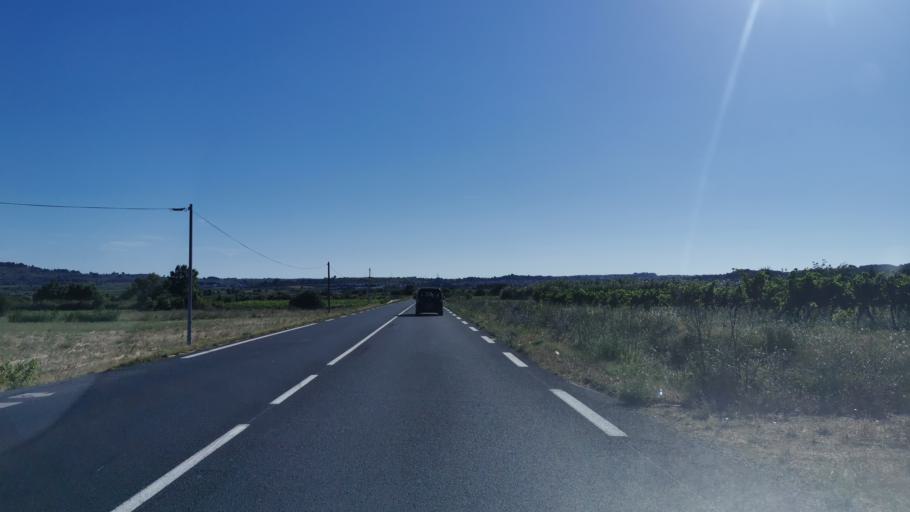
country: FR
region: Languedoc-Roussillon
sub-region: Departement de l'Herault
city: Nissan-lez-Enserune
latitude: 43.2782
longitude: 3.0953
